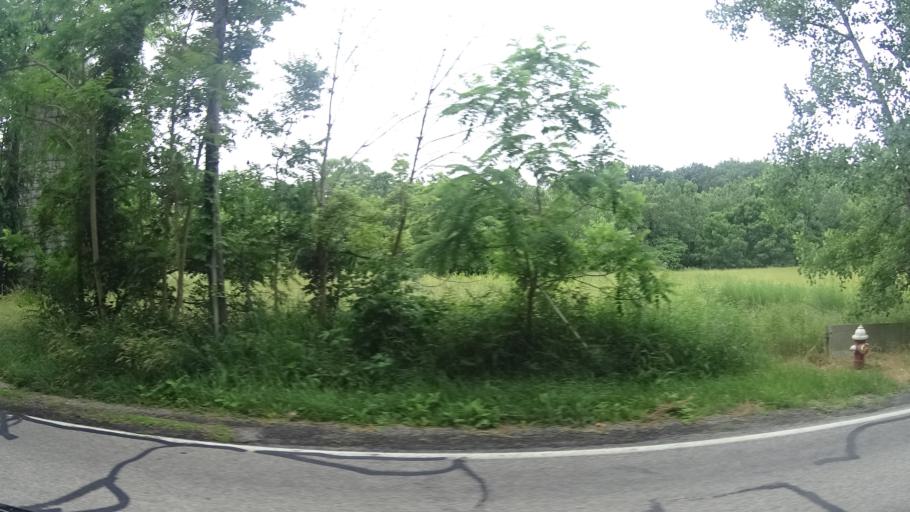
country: US
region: Ohio
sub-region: Erie County
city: Huron
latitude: 41.3270
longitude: -82.5027
